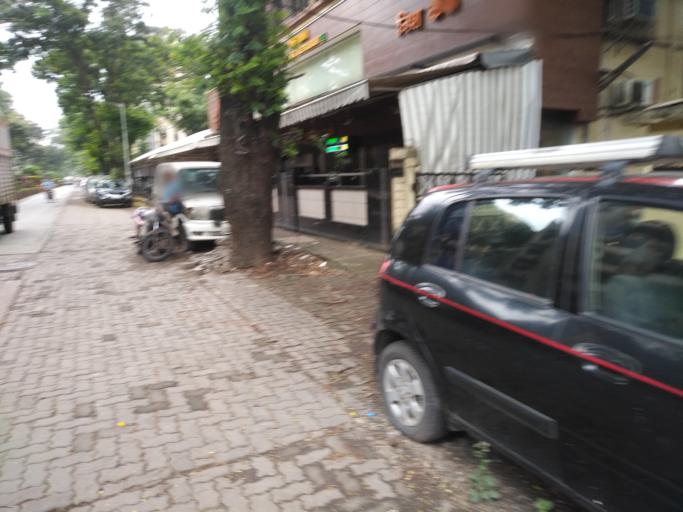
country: IN
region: Maharashtra
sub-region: Mumbai Suburban
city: Borivli
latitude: 19.2436
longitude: 72.8652
